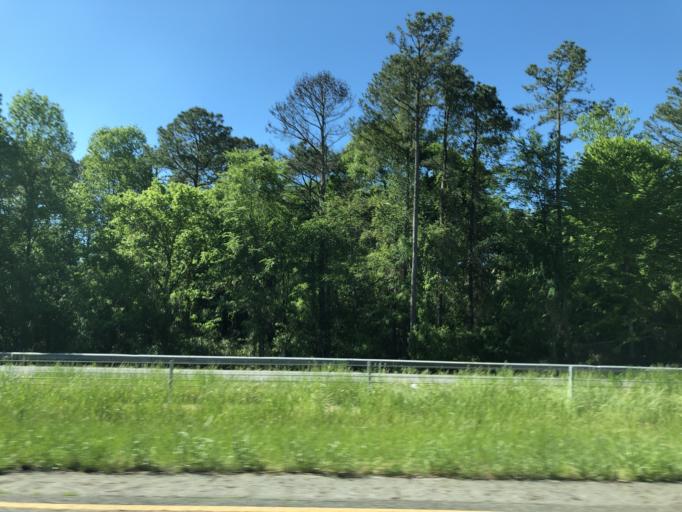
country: US
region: Georgia
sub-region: Clarke County
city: Country Club Estates
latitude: 33.9494
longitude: -83.4445
